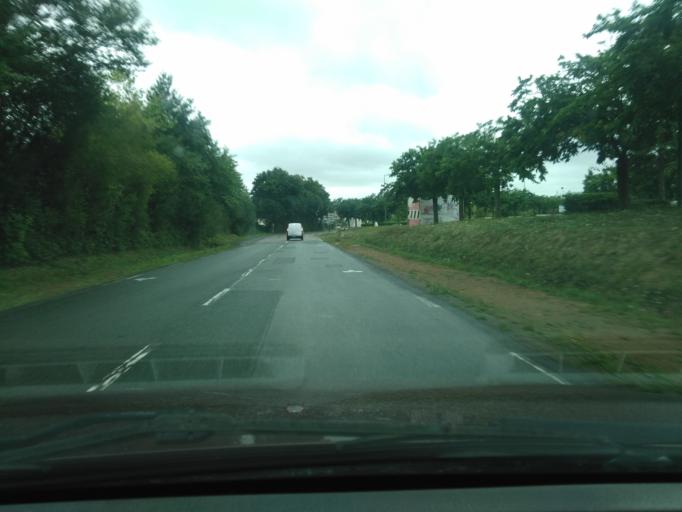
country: FR
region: Pays de la Loire
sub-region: Departement de la Vendee
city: La Roche-sur-Yon
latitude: 46.6764
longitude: -1.4031
